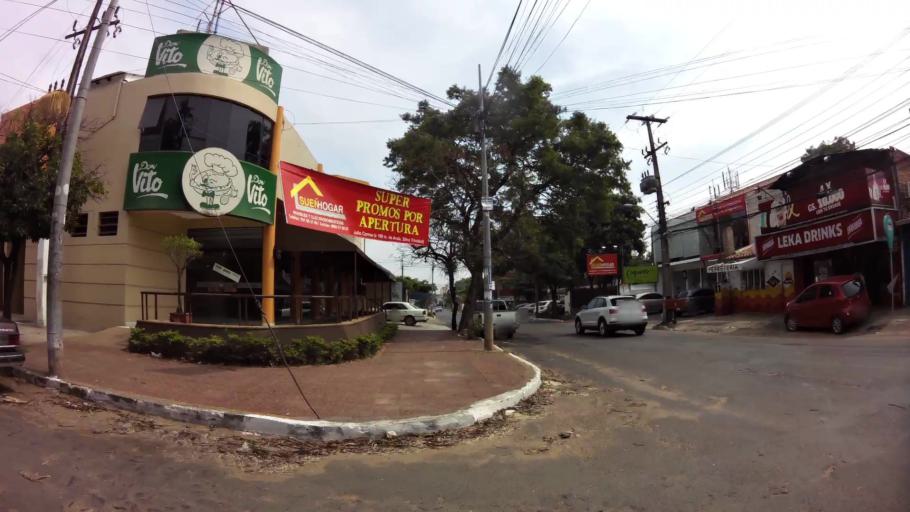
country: PY
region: Asuncion
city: Asuncion
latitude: -25.2705
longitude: -57.5641
